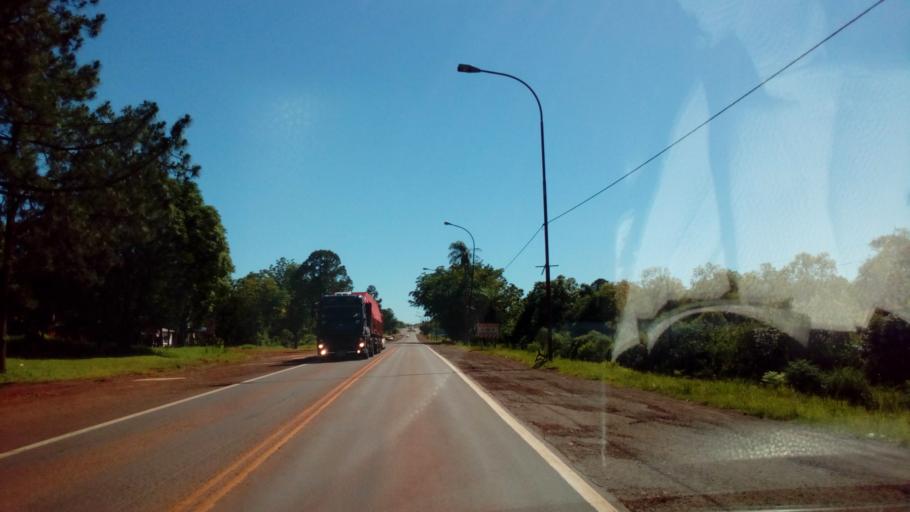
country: AR
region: Misiones
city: Santa Ana
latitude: -27.3813
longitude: -55.5840
